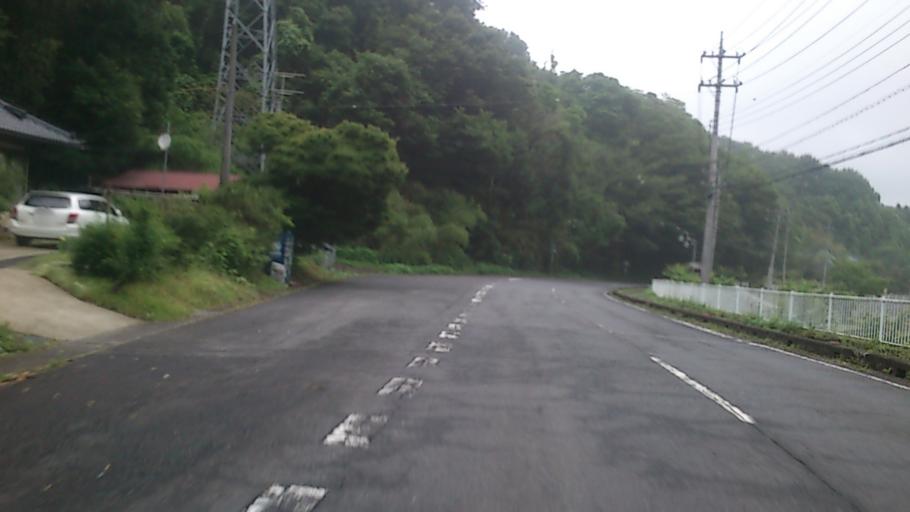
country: JP
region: Ibaraki
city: Omiya
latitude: 36.6295
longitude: 140.3696
